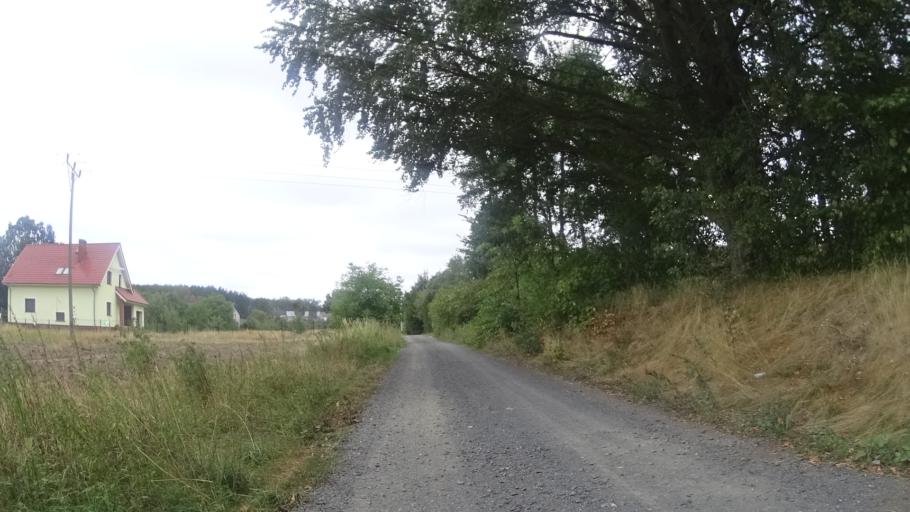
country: PL
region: Lubusz
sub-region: Powiat zarski
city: Przewoz
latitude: 51.4772
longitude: 14.9450
